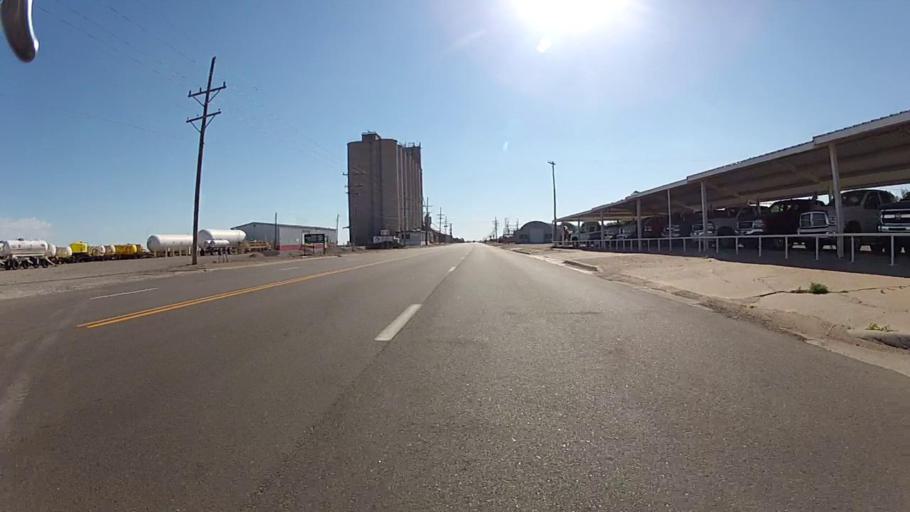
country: US
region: Kansas
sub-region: Haskell County
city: Sublette
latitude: 37.5428
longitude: -100.6294
